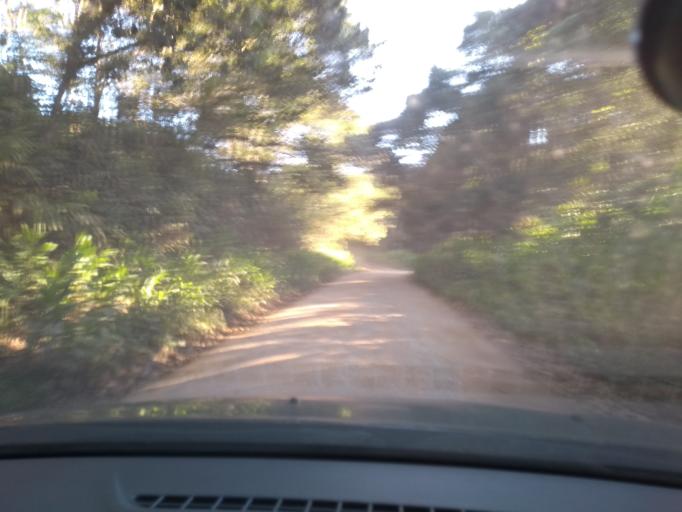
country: BR
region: Sao Paulo
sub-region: Rio Grande Da Serra
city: Rio Grande da Serra
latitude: -23.7783
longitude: -46.4895
